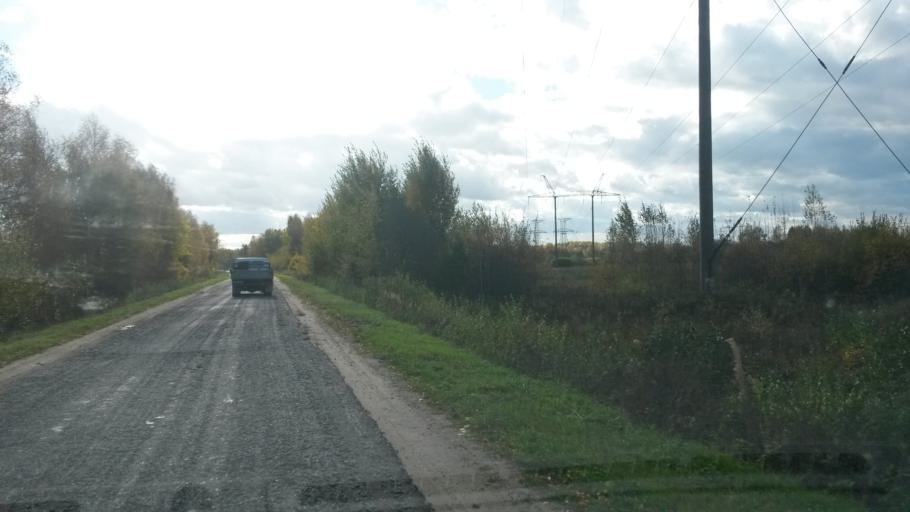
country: RU
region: Jaroslavl
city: Tunoshna
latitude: 57.5344
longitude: 40.0181
